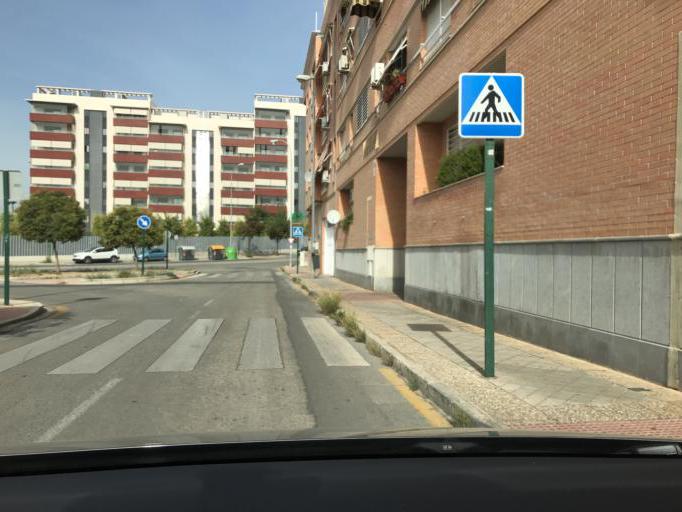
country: ES
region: Andalusia
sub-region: Provincia de Granada
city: Granada
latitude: 37.1978
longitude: -3.6173
